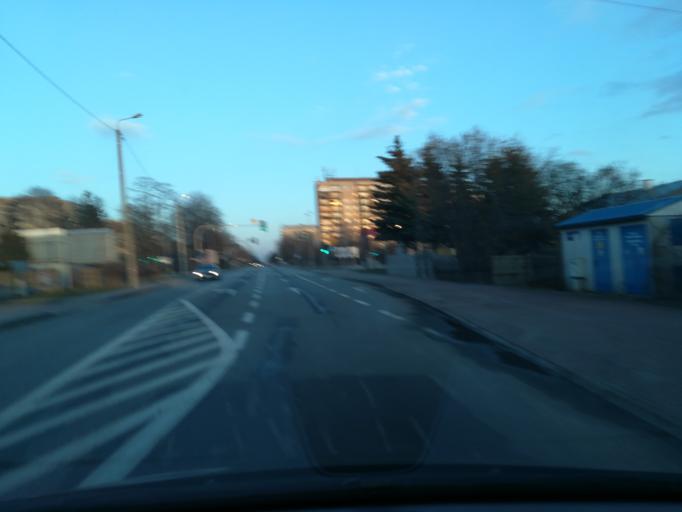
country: PL
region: Lodz Voivodeship
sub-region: Piotrkow Trybunalski
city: Piotrkow Trybunalski
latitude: 51.4107
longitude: 19.6551
